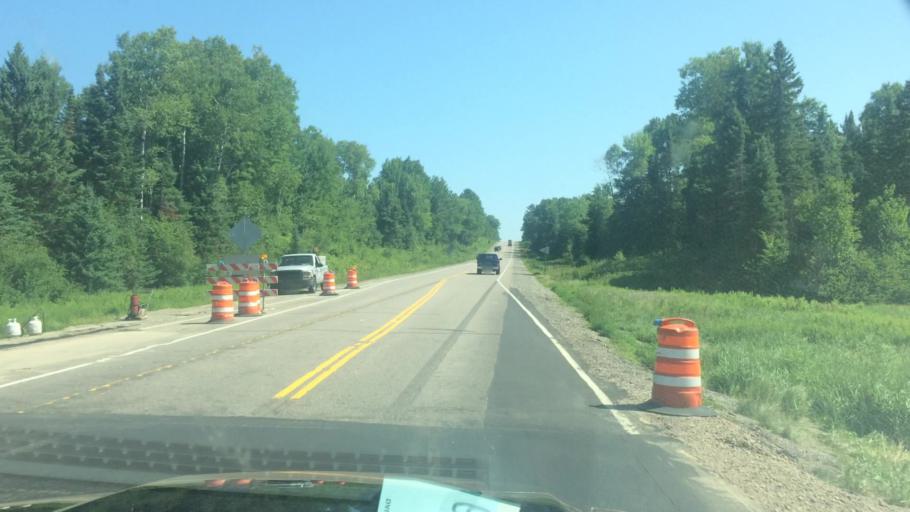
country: US
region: Wisconsin
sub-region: Lincoln County
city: Tomahawk
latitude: 45.5476
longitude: -89.6617
